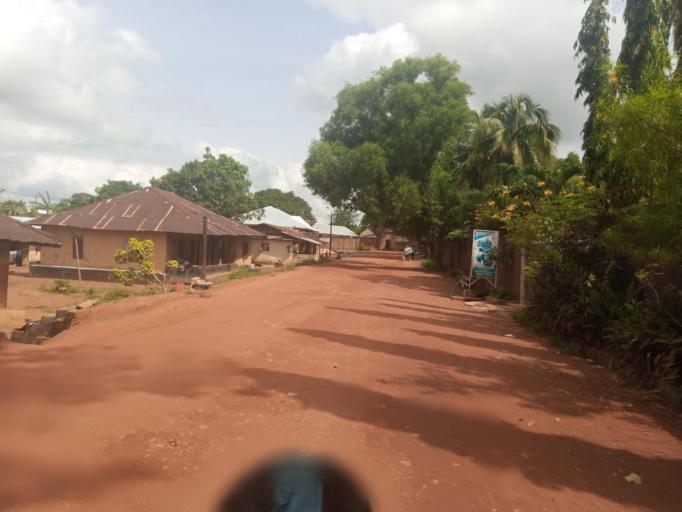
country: SL
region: Southern Province
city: Bo
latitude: 7.9677
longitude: -11.7422
